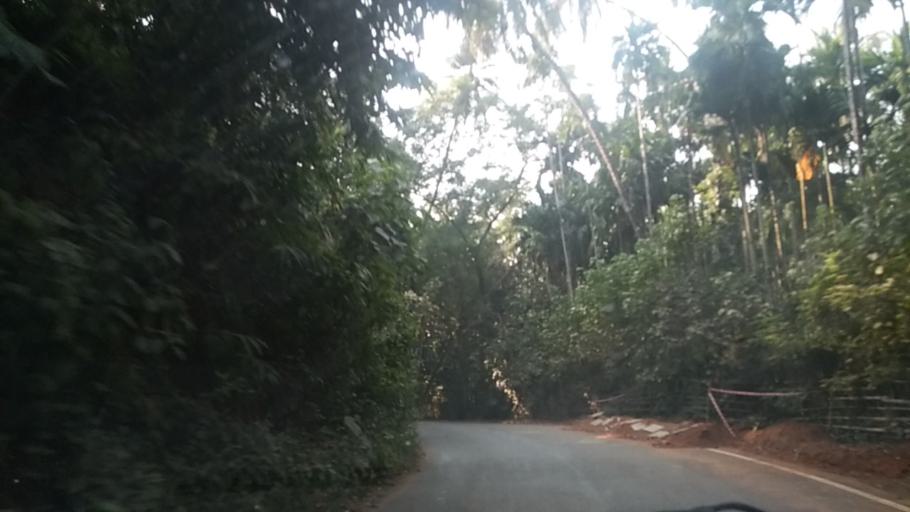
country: IN
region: Goa
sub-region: North Goa
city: Pernem
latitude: 15.7264
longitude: 73.7745
